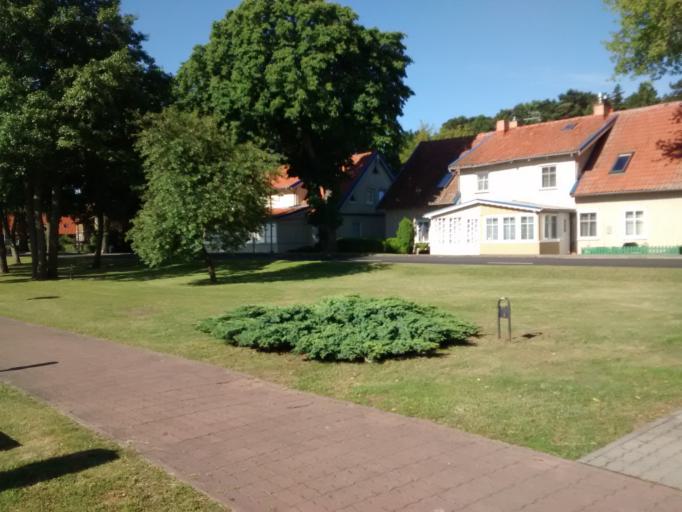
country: LT
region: Klaipedos apskritis
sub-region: Klaipeda
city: Klaipeda
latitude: 55.5402
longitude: 21.1199
